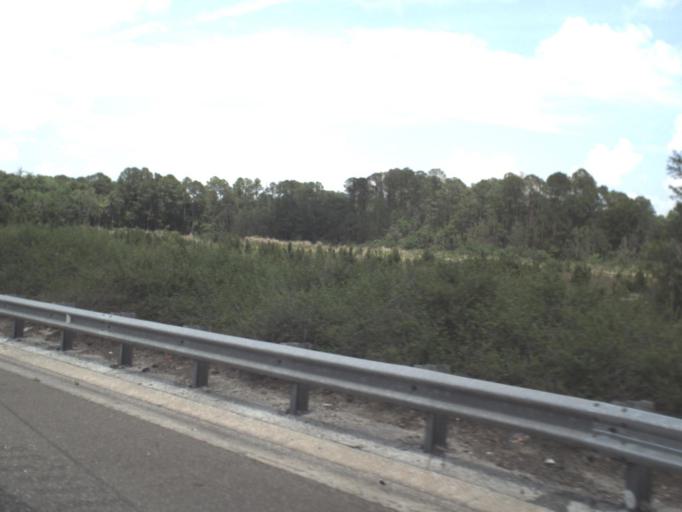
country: US
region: Florida
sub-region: Duval County
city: Jacksonville
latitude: 30.3382
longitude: -81.7606
